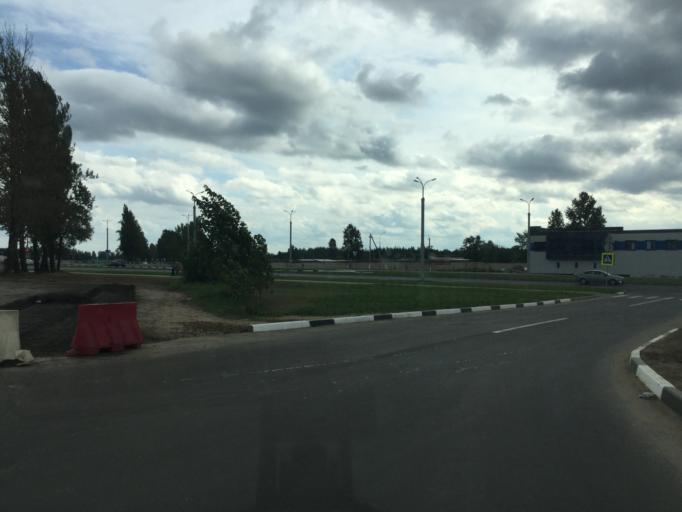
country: BY
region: Vitebsk
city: Vitebsk
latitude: 55.1676
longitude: 30.2526
